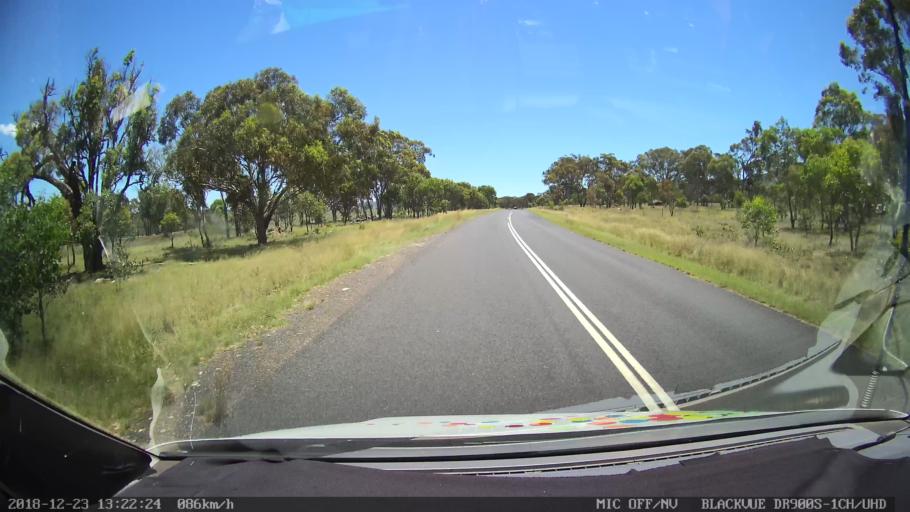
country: AU
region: New South Wales
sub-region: Armidale Dumaresq
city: Armidale
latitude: -30.4793
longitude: 151.4216
